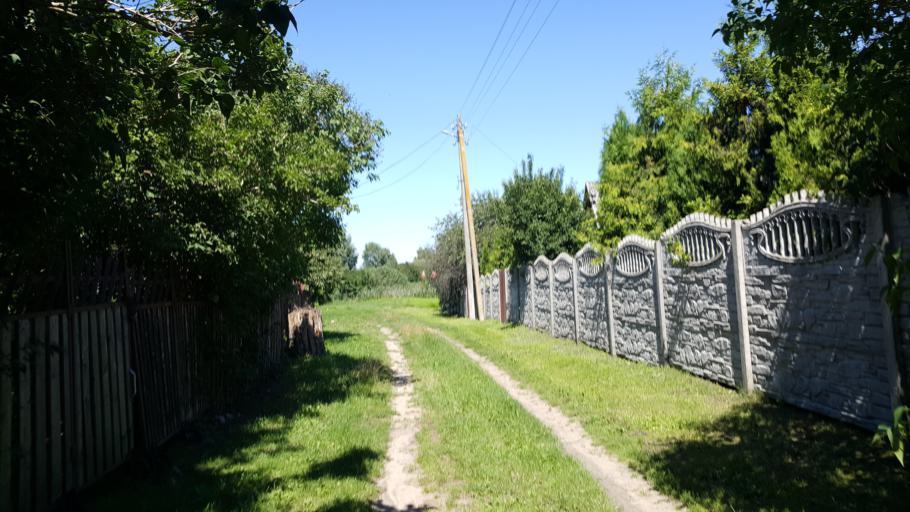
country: BY
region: Brest
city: Charnawchytsy
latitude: 52.2342
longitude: 23.7787
